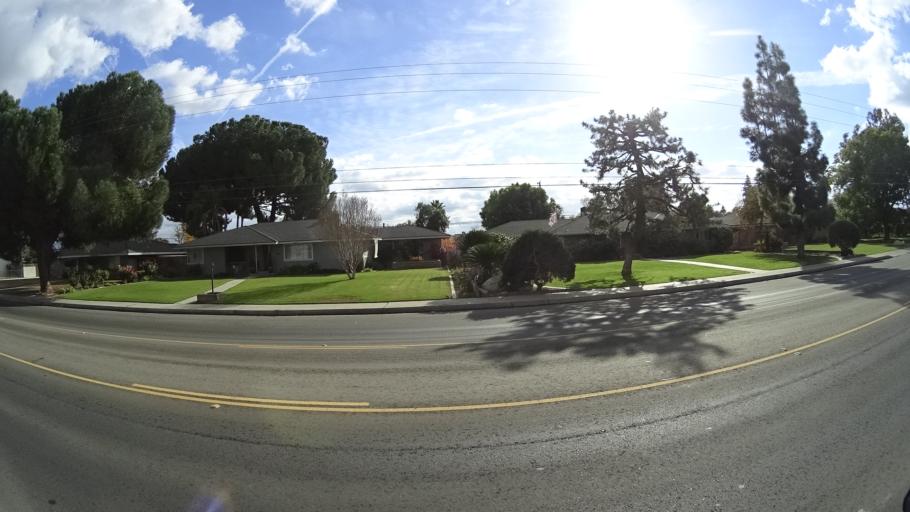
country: US
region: California
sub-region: Kern County
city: Bakersfield
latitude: 35.3322
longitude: -119.0276
